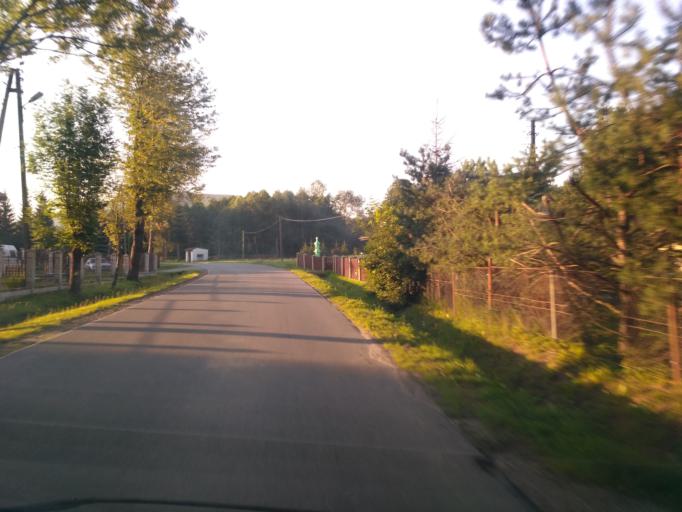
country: PL
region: Subcarpathian Voivodeship
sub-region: Powiat krosnienski
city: Odrzykon
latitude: 49.7725
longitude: 21.7825
